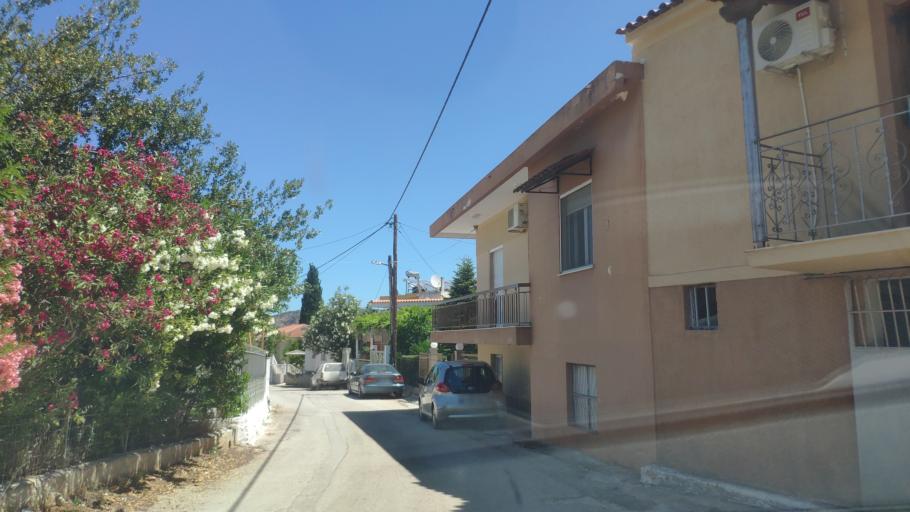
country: GR
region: Peloponnese
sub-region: Nomos Korinthias
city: Athikia
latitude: 37.8149
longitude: 22.9233
